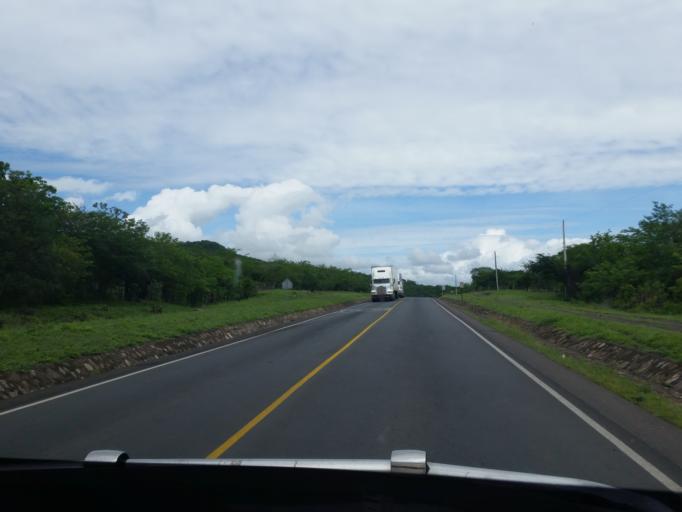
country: NI
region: Matagalpa
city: Ciudad Dario
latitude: 12.6045
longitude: -86.0458
